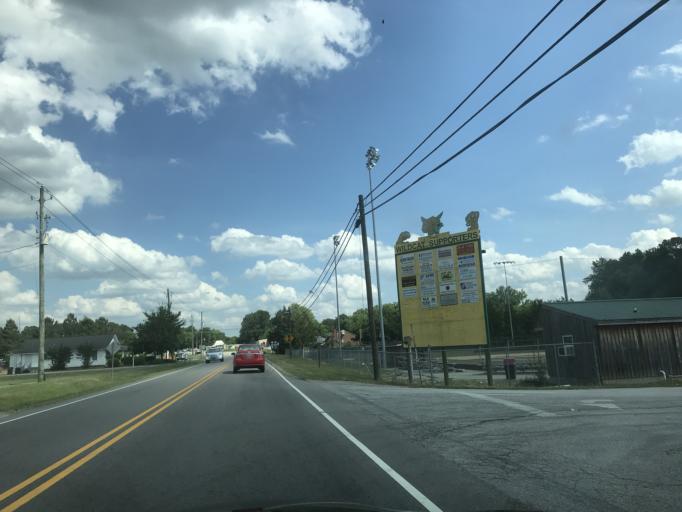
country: US
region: North Carolina
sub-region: Nash County
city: Spring Hope
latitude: 35.9550
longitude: -78.2475
